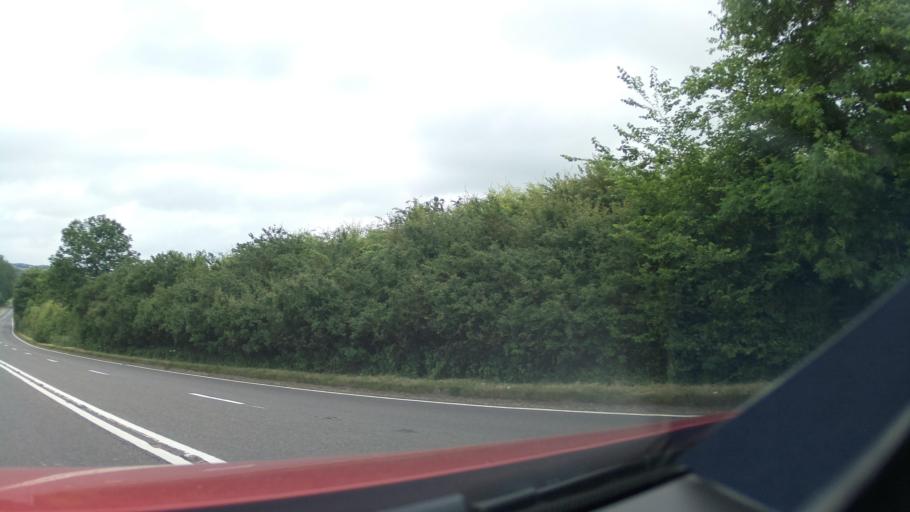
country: GB
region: England
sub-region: Leicestershire
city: Houghton on the Hill
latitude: 52.6257
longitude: -0.9817
